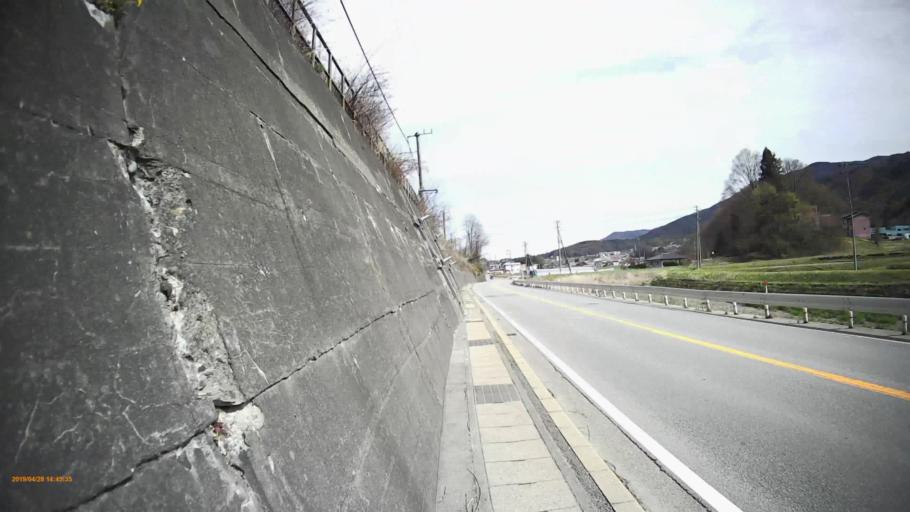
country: JP
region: Nagano
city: Chino
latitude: 35.9603
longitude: 138.1791
